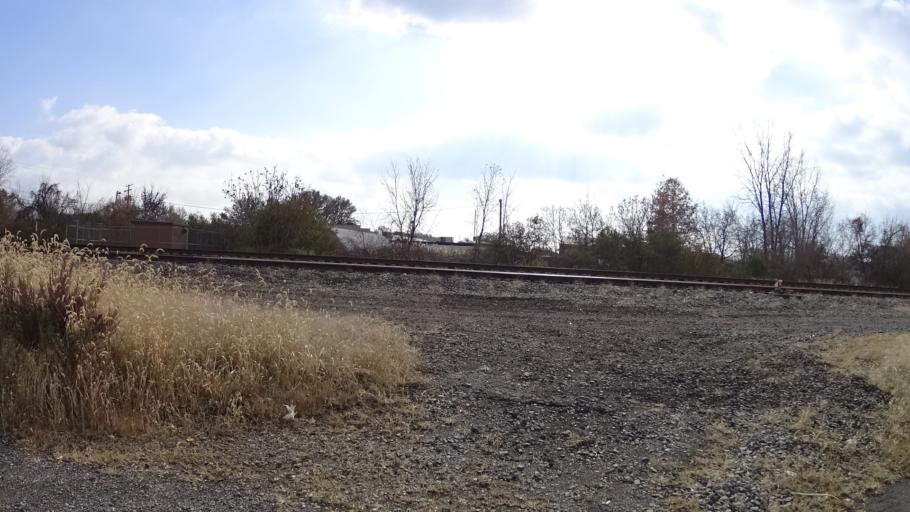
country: US
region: Ohio
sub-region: Lorain County
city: Elyria
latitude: 41.3742
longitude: -82.0787
